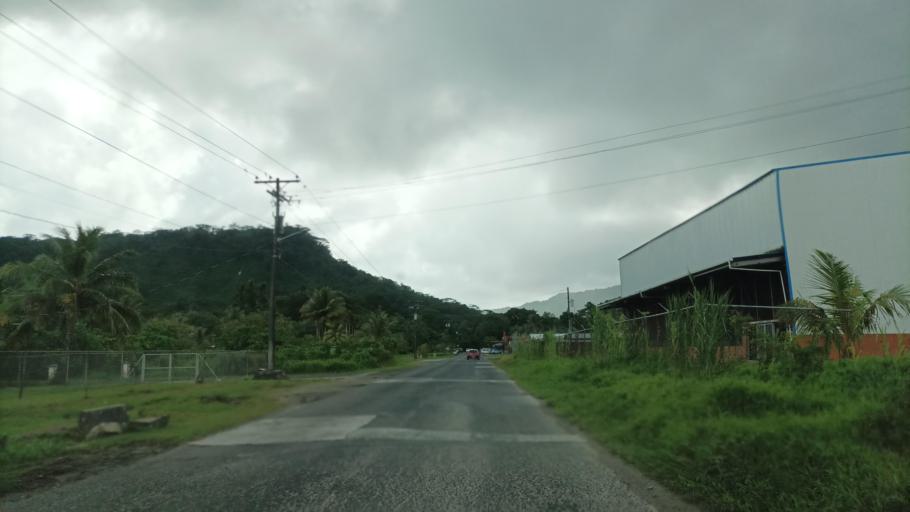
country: FM
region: Pohnpei
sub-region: Kolonia Municipality
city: Kolonia
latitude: 6.9541
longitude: 158.2202
